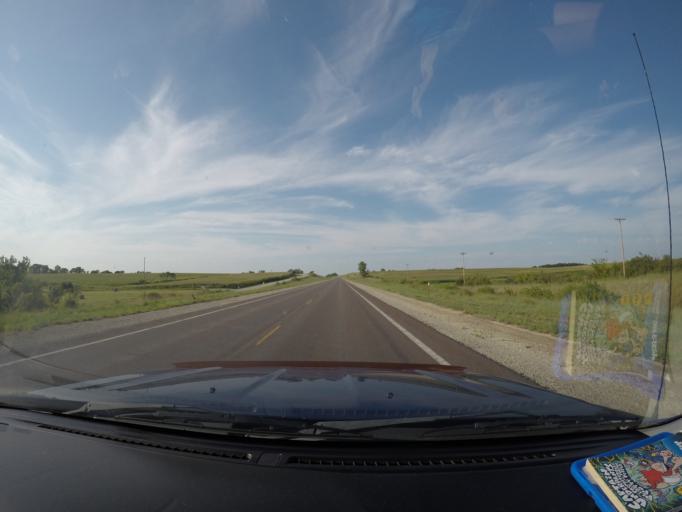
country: US
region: Kansas
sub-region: Atchison County
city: Atchison
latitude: 39.4131
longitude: -95.0666
